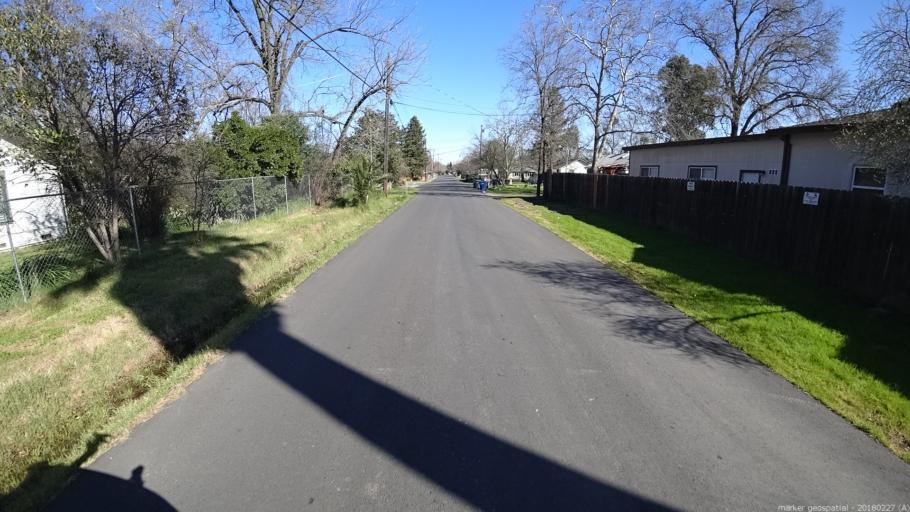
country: US
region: California
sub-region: Sacramento County
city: Rio Linda
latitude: 38.6929
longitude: -121.4474
